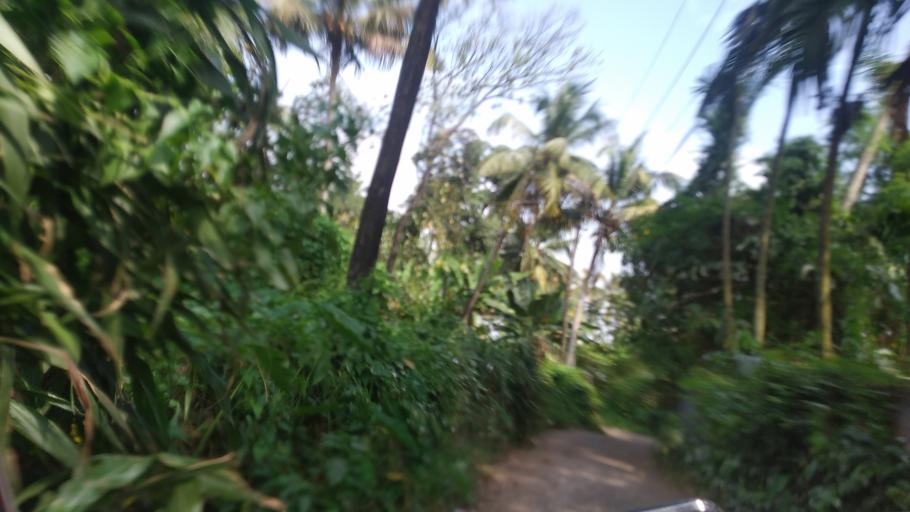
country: IN
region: Kerala
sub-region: Ernakulam
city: Elur
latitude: 10.0826
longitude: 76.2197
